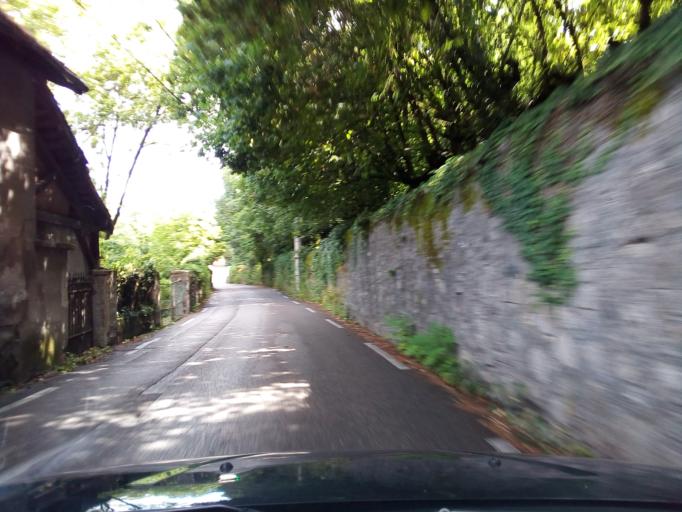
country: FR
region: Rhone-Alpes
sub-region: Departement de l'Isere
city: Saint-Martin-d'Heres
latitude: 45.1749
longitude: 5.7722
